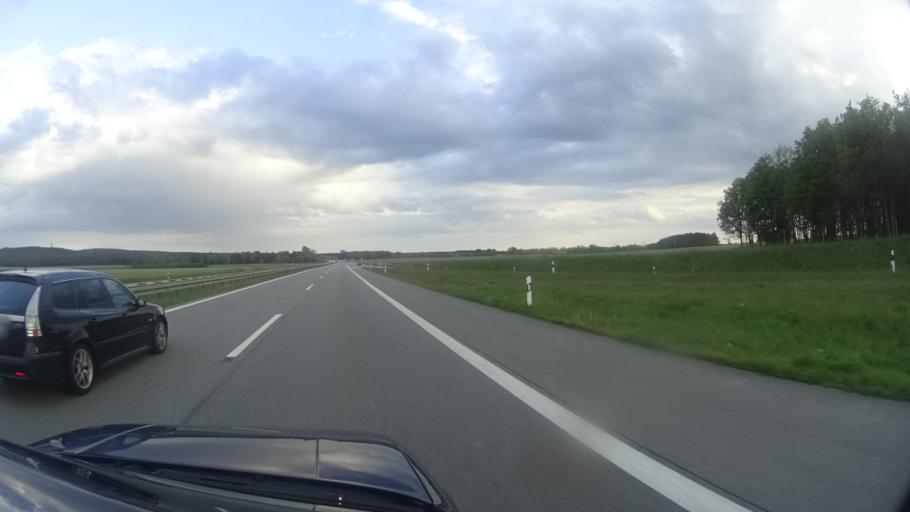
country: DE
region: Brandenburg
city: Wittstock
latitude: 53.1319
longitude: 12.4590
